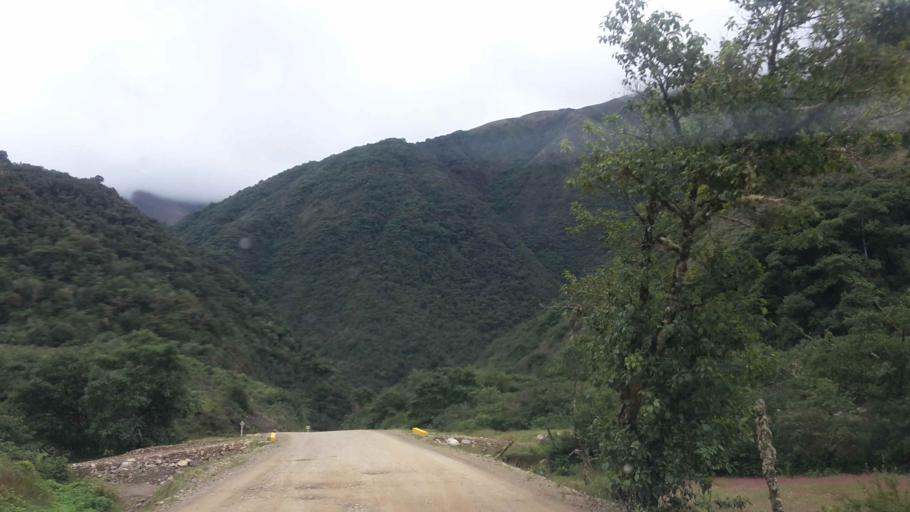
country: BO
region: Cochabamba
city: Totora
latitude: -17.5615
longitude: -65.2746
